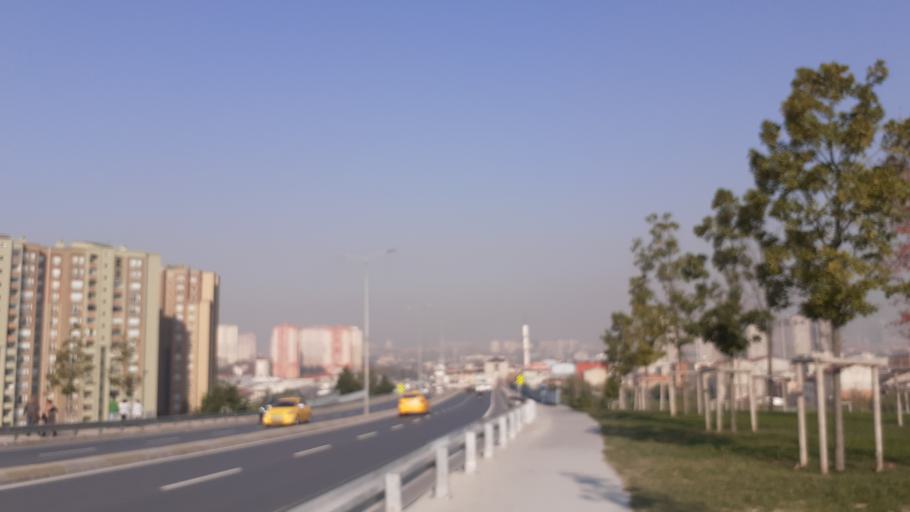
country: TR
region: Istanbul
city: Mahmutbey
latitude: 41.0496
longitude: 28.7940
